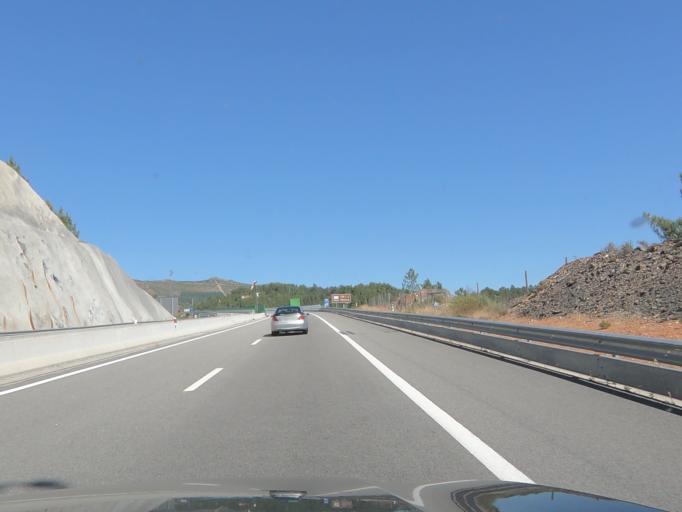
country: PT
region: Vila Real
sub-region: Murca
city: Murca
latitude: 41.4099
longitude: -7.4175
